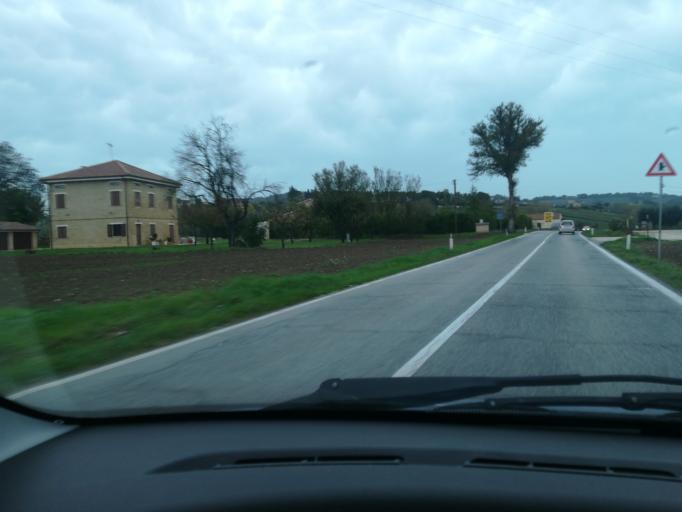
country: IT
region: The Marches
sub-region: Provincia di Macerata
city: Borgo Stazione
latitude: 43.2928
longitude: 13.6631
